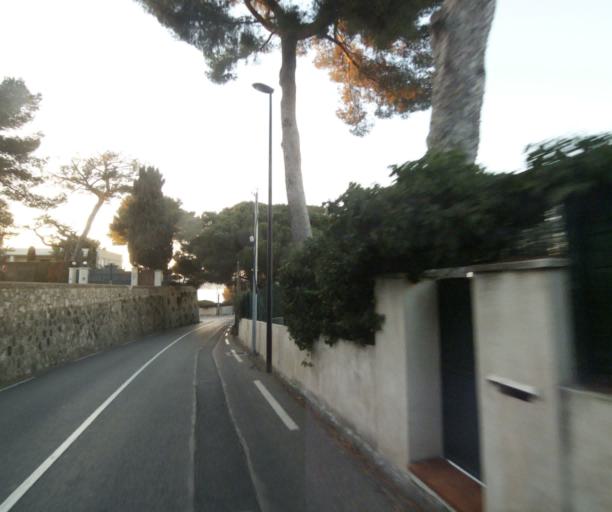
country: FR
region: Provence-Alpes-Cote d'Azur
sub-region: Departement des Alpes-Maritimes
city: Antibes
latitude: 43.5493
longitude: 7.1202
